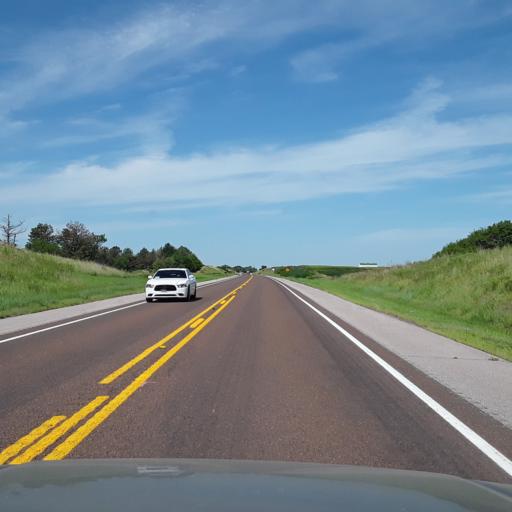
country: US
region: Nebraska
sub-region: Lancaster County
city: Lincoln
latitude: 40.8868
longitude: -96.8522
